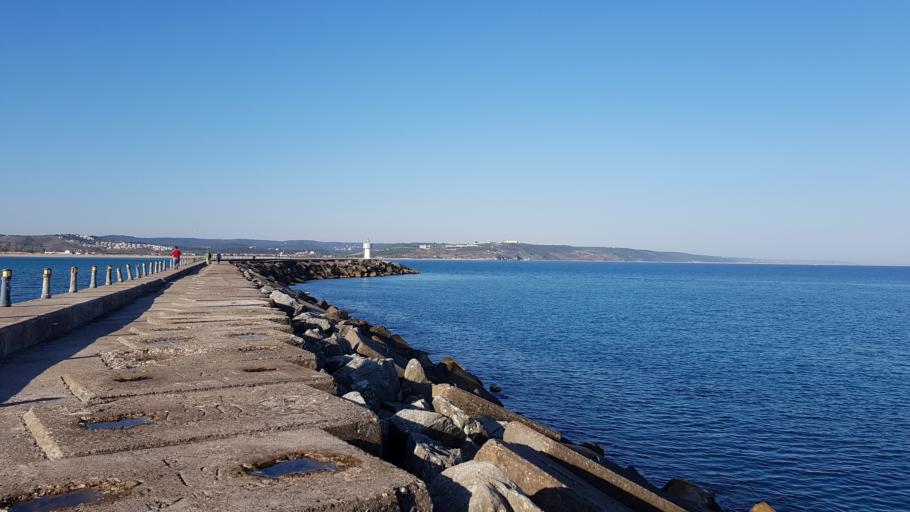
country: TR
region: Istanbul
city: Sile
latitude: 41.1799
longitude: 29.6035
